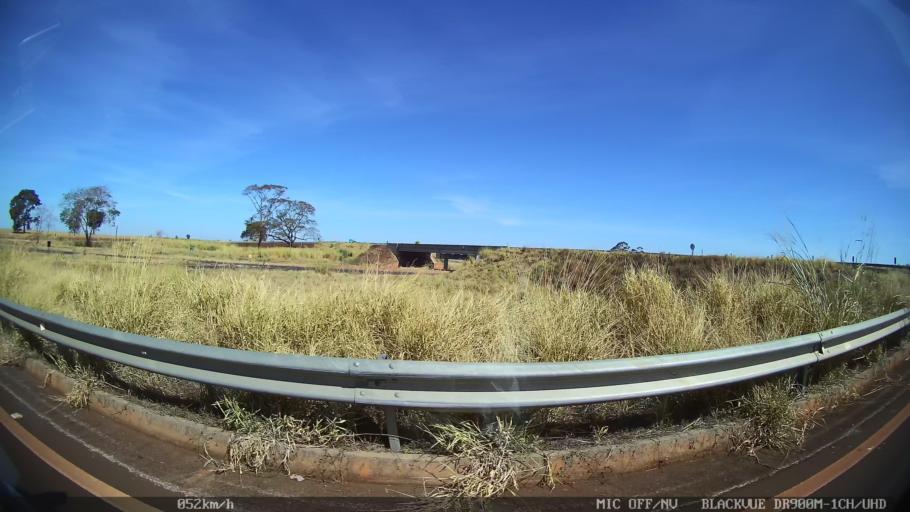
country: BR
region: Sao Paulo
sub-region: Nuporanga
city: Nuporanga
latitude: -20.5602
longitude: -47.6246
